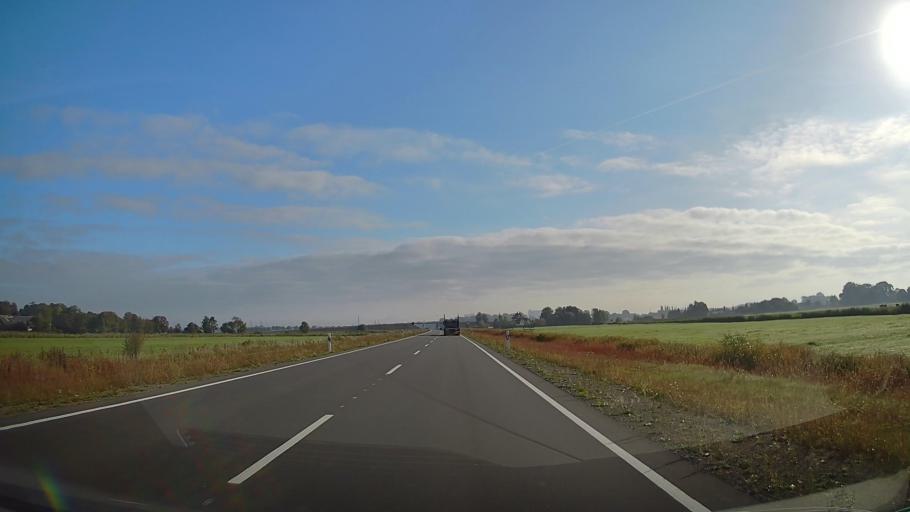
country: DE
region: Lower Saxony
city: Ovelgonne
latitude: 53.3260
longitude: 8.4369
